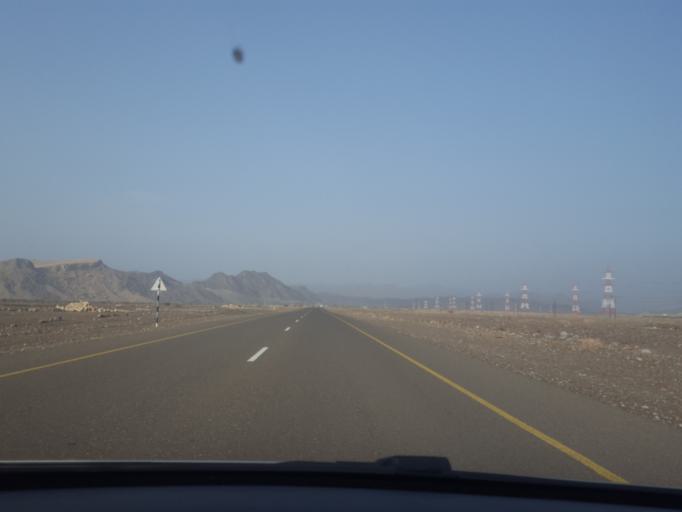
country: AE
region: Abu Dhabi
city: Al Ain
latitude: 24.0430
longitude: 56.0309
